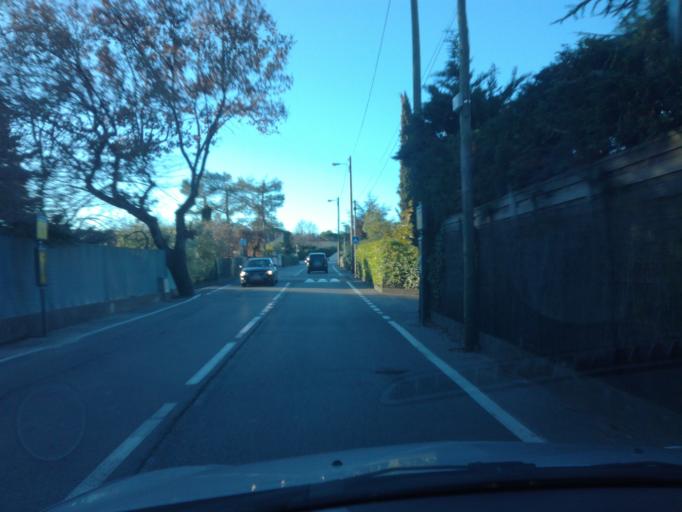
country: FR
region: Provence-Alpes-Cote d'Azur
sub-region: Departement des Alpes-Maritimes
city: La Roquette-sur-Siagne
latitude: 43.6087
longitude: 6.9672
